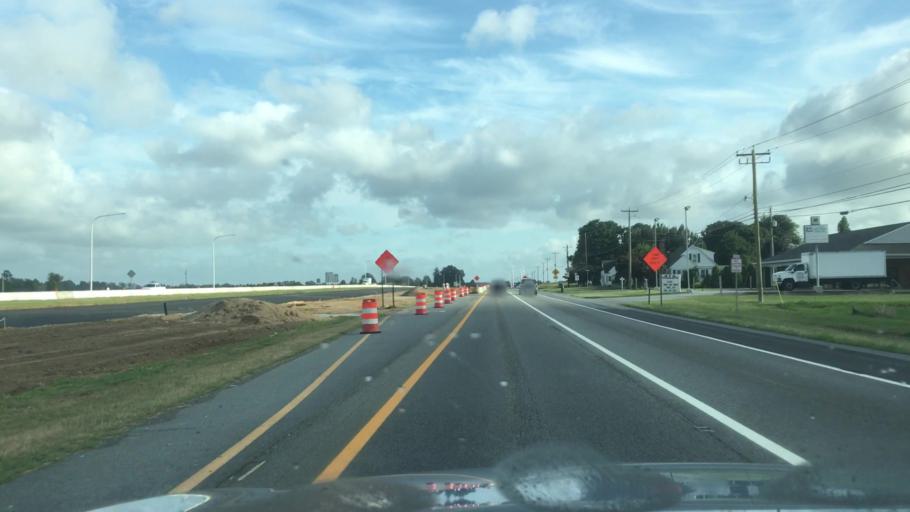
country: US
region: Delaware
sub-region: Kent County
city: Riverview
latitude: 39.0339
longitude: -75.4584
